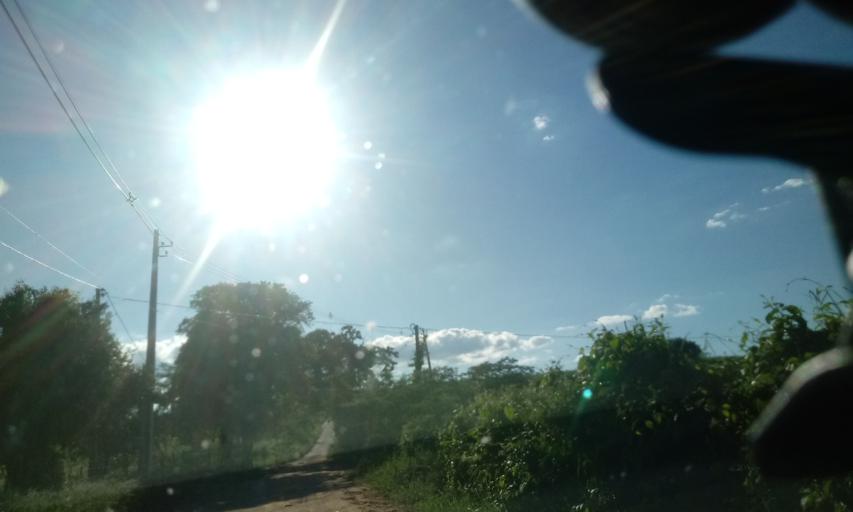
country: BR
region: Bahia
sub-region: Riacho De Santana
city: Riacho de Santana
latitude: -13.7999
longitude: -42.7444
